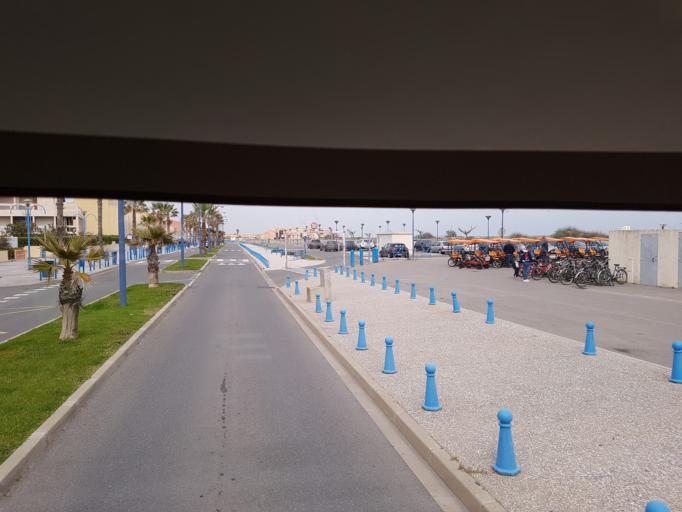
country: FR
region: Languedoc-Roussillon
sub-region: Departement de l'Aude
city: Fleury
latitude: 43.1790
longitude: 3.1906
